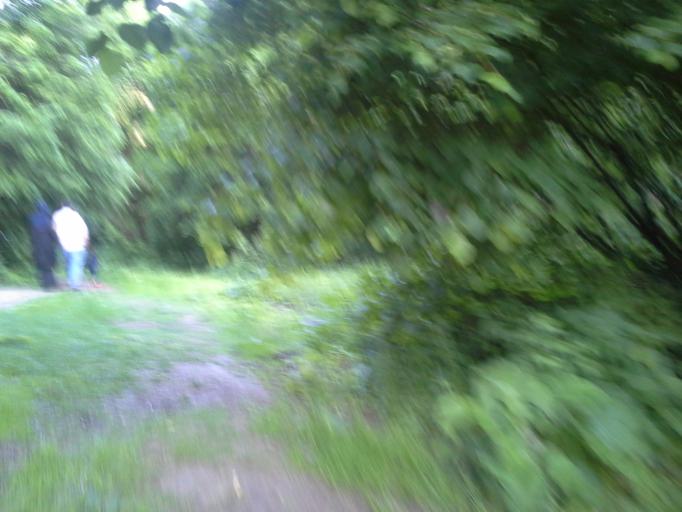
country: RU
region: Moskovskaya
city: Vostryakovo
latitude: 55.6638
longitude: 37.4572
